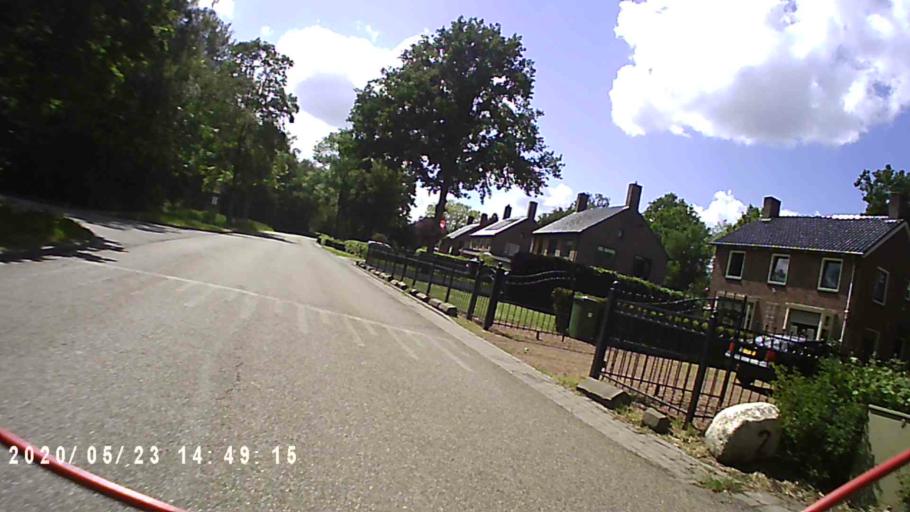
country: NL
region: Groningen
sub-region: Gemeente Delfzijl
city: Delfzijl
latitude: 53.2591
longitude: 6.9425
